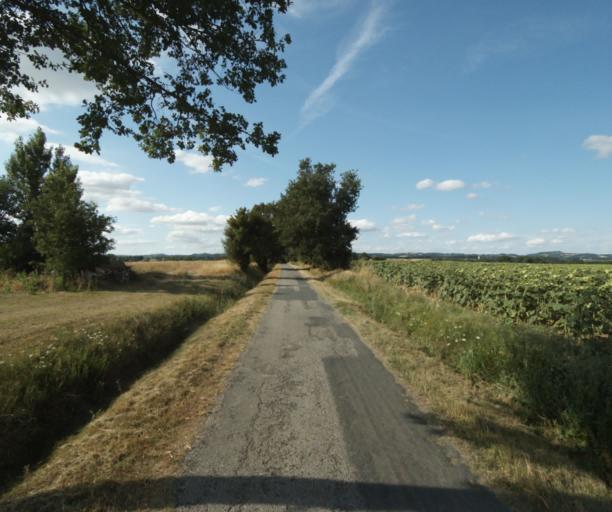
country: FR
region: Midi-Pyrenees
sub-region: Departement de la Haute-Garonne
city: Revel
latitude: 43.5080
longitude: 1.9971
